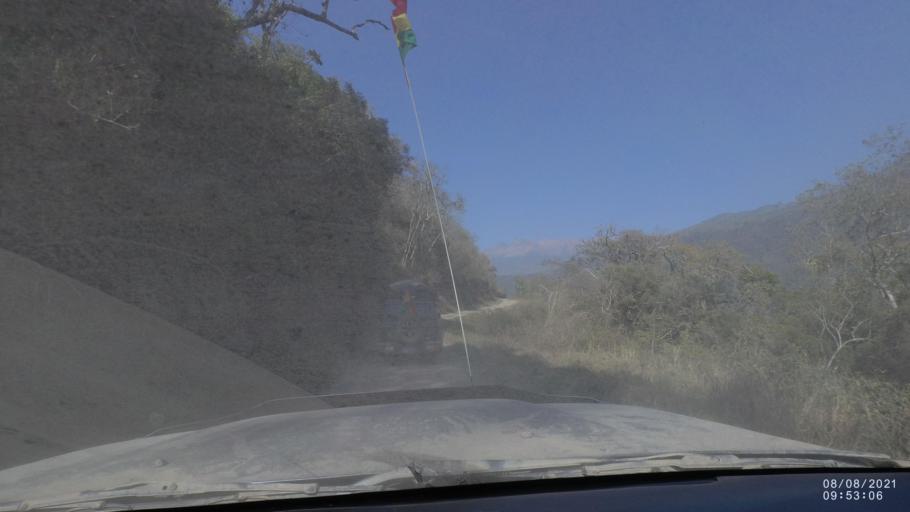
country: BO
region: La Paz
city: Quime
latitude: -16.6272
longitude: -66.7320
